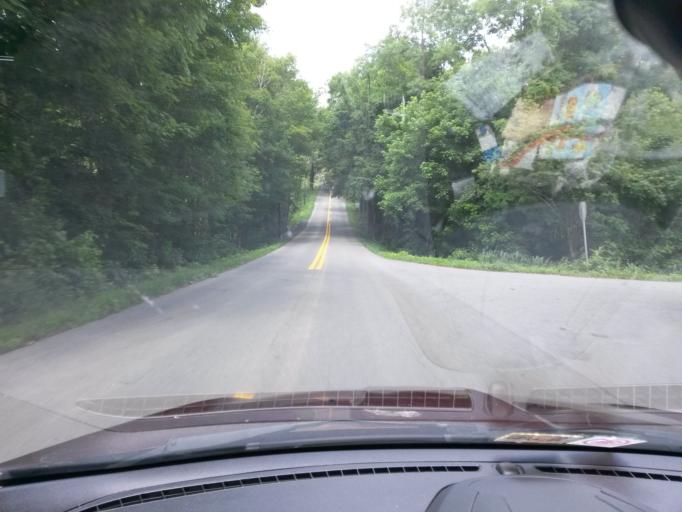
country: US
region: West Virginia
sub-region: Monroe County
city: Union
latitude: 37.5558
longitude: -80.5222
